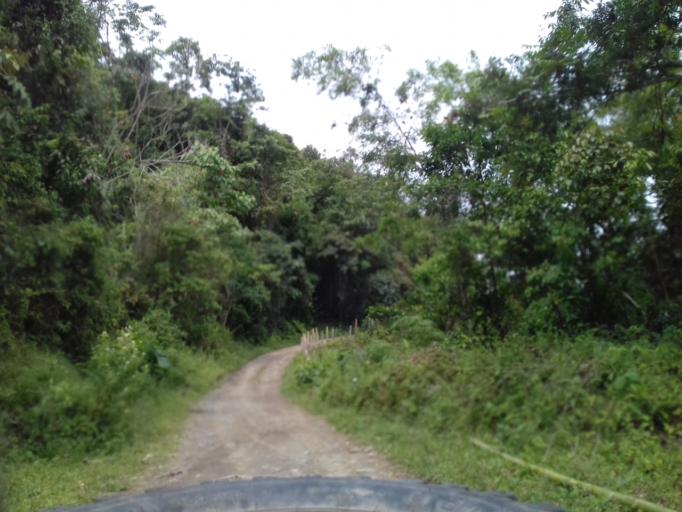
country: CO
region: Tolima
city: Libano
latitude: 4.9280
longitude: -75.0889
